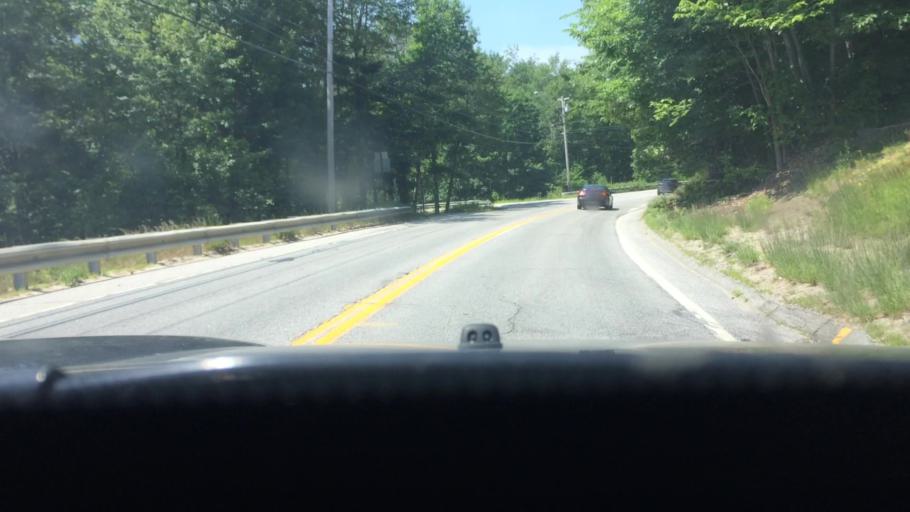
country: US
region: Maine
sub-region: Androscoggin County
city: Mechanic Falls
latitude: 44.1110
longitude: -70.4158
